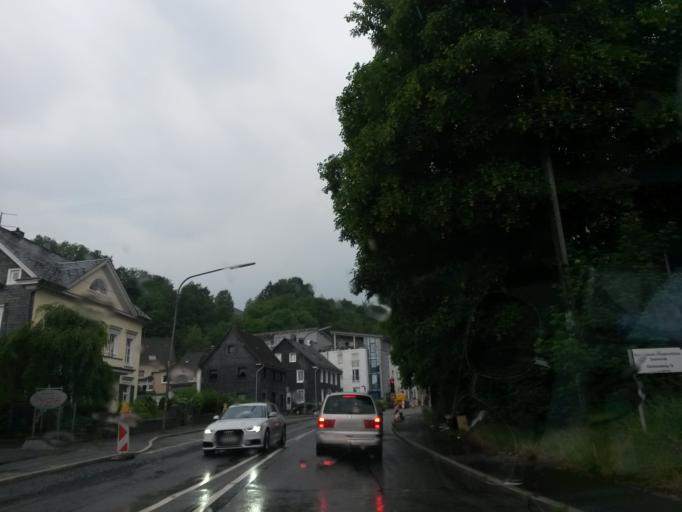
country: DE
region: North Rhine-Westphalia
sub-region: Regierungsbezirk Koln
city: Gummersbach
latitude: 51.0286
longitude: 7.5605
